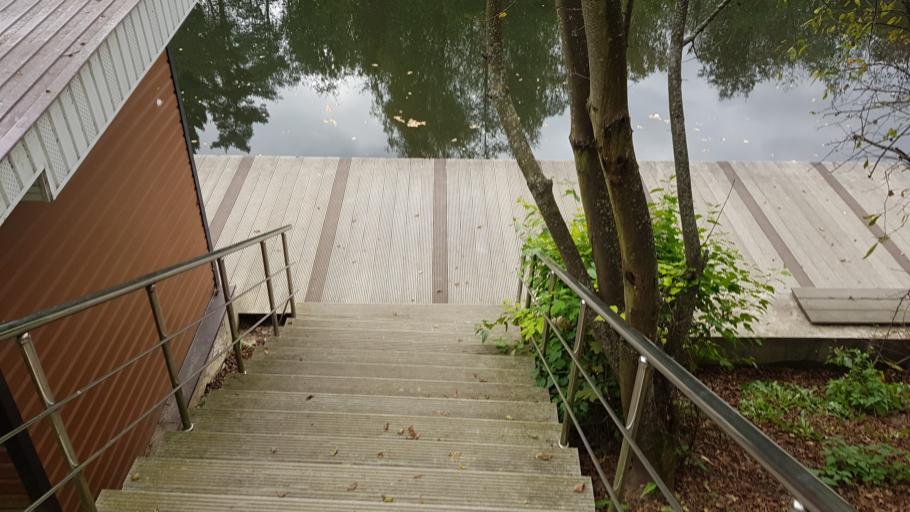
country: RU
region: Moskovskaya
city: Filimonki
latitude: 55.5205
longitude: 37.4057
